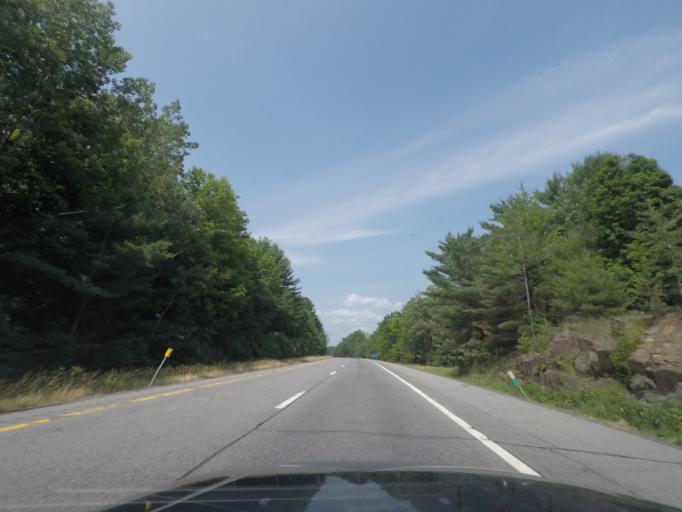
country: US
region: New York
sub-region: Warren County
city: Warrensburg
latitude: 43.7658
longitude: -73.8035
